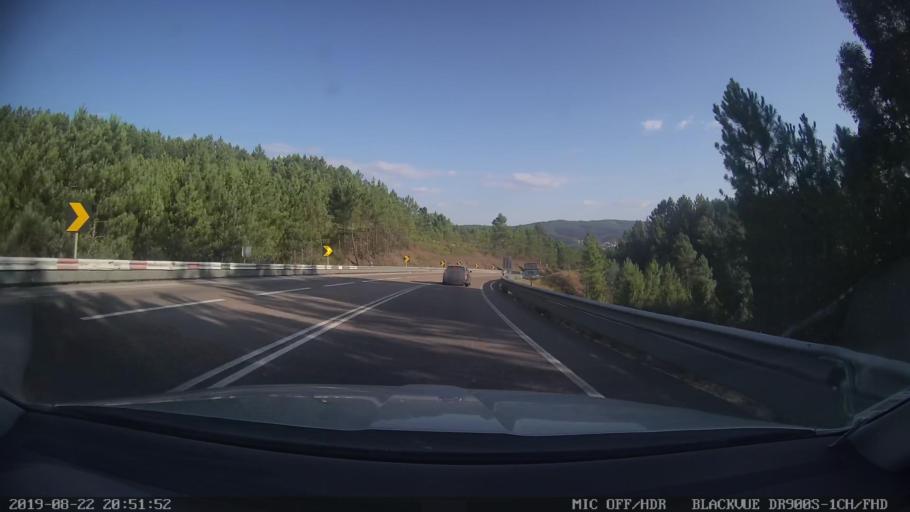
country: PT
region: Castelo Branco
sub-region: Proenca-A-Nova
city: Proenca-a-Nova
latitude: 39.7637
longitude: -7.9666
